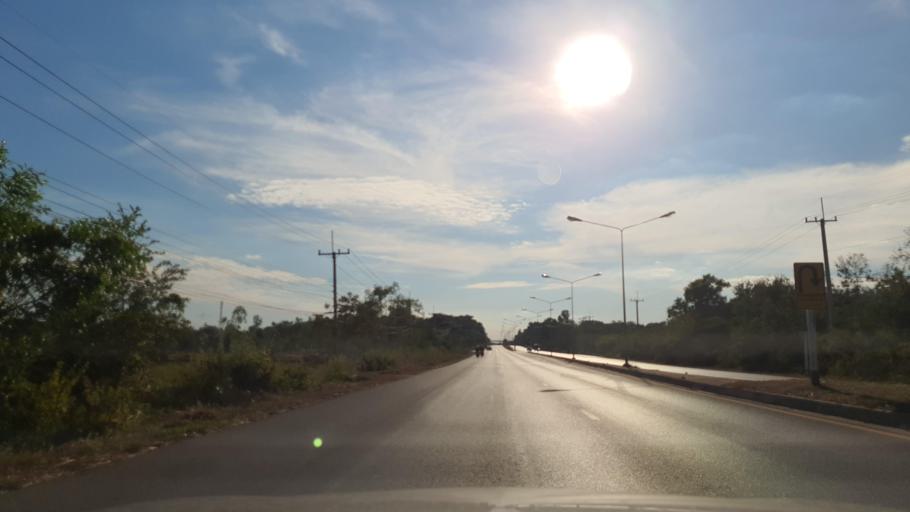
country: TH
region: Maha Sarakham
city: Kantharawichai
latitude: 16.3360
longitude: 103.3091
